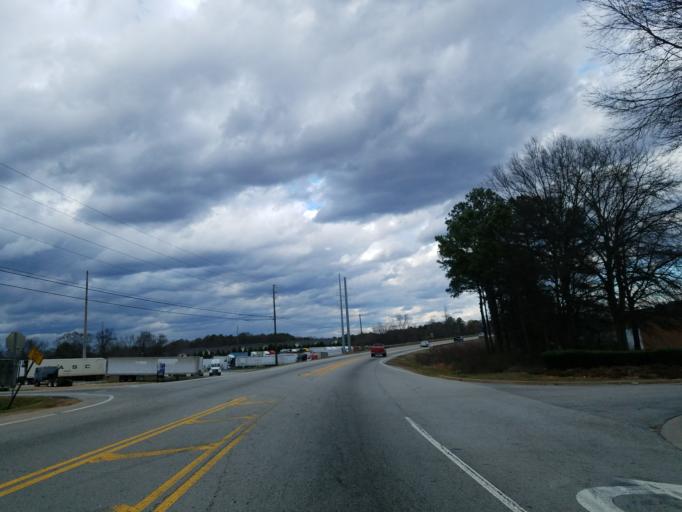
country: US
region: Georgia
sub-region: Henry County
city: McDonough
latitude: 33.4236
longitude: -84.1519
